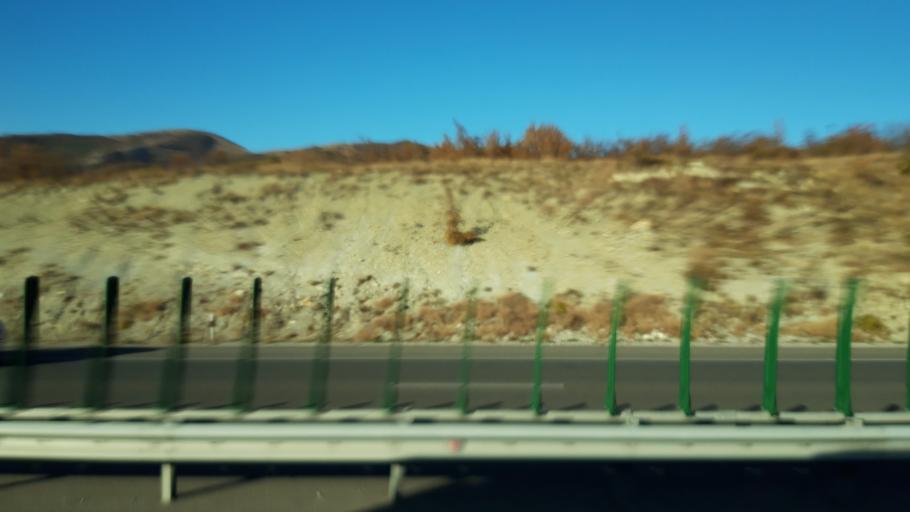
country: RU
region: Krasnodarskiy
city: Kabardinka
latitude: 44.6416
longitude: 37.9755
